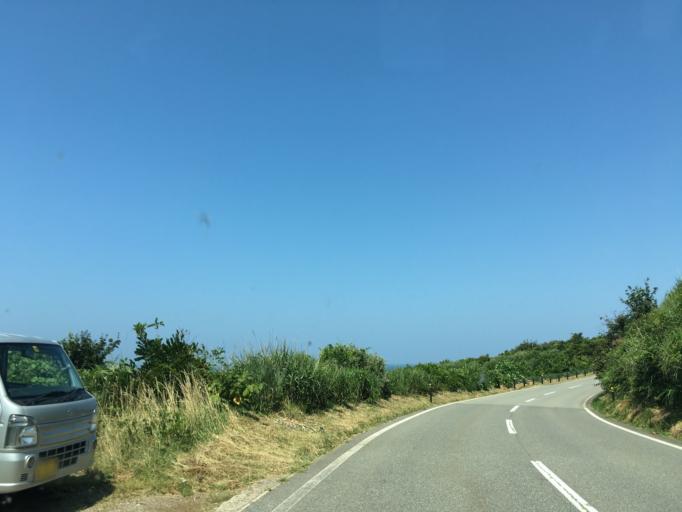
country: JP
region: Akita
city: Tenno
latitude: 39.9233
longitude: 139.7133
